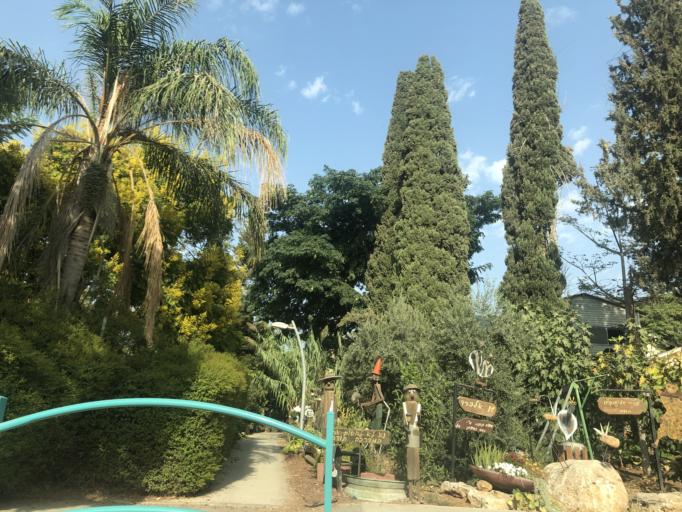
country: IL
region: Central District
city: Rosh Ha'Ayin
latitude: 32.0823
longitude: 34.9357
